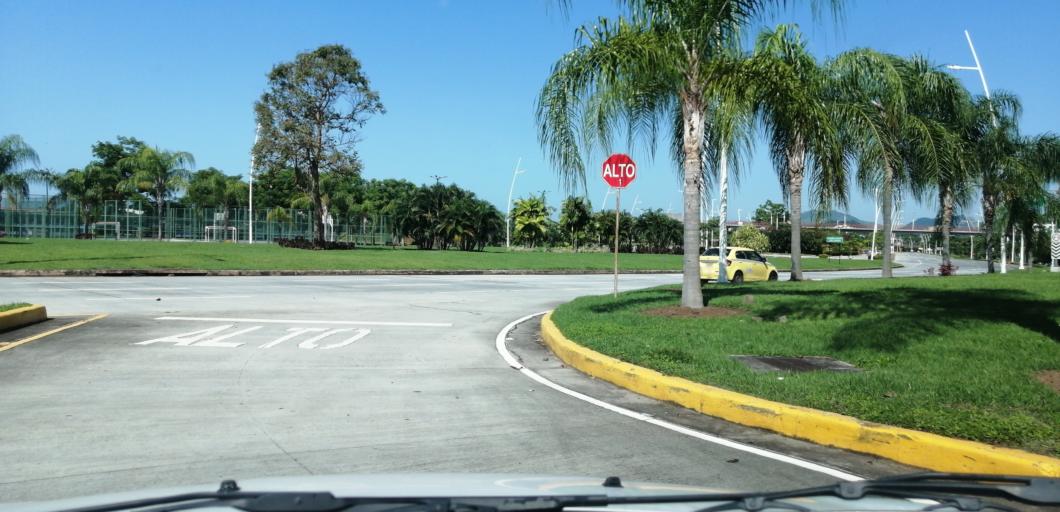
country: PA
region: Panama
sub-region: Distrito de Panama
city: Ancon
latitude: 8.9494
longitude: -79.5405
